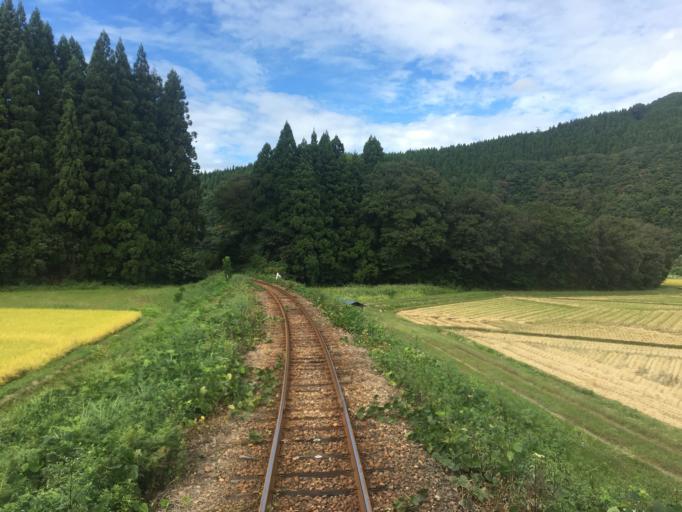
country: JP
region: Yamagata
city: Yuza
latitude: 39.2635
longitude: 140.1261
